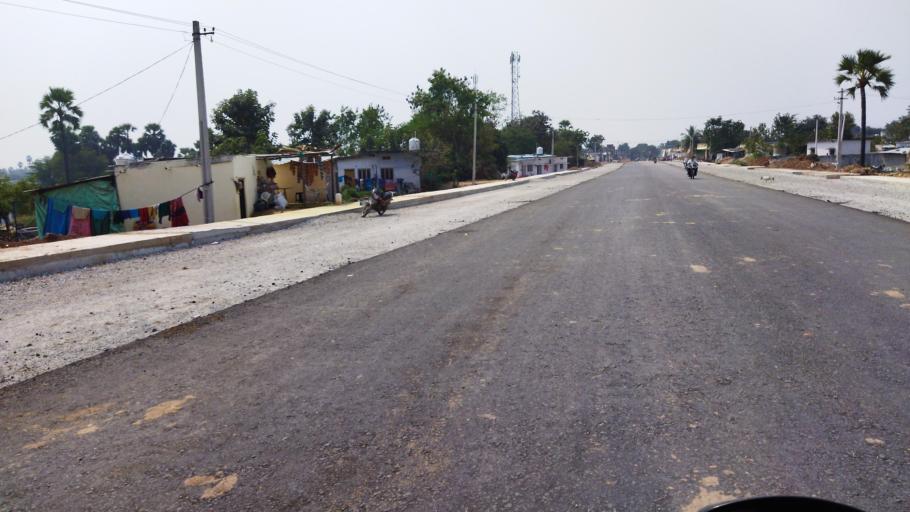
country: IN
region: Telangana
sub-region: Nalgonda
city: Nalgonda
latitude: 17.1453
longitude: 79.3959
